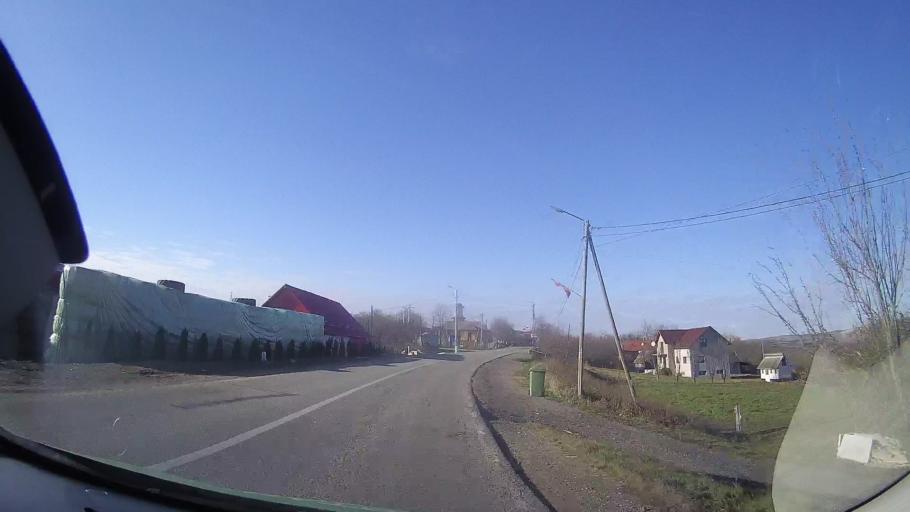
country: RO
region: Cluj
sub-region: Comuna Mociu
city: Mociu
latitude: 46.7901
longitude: 24.0752
